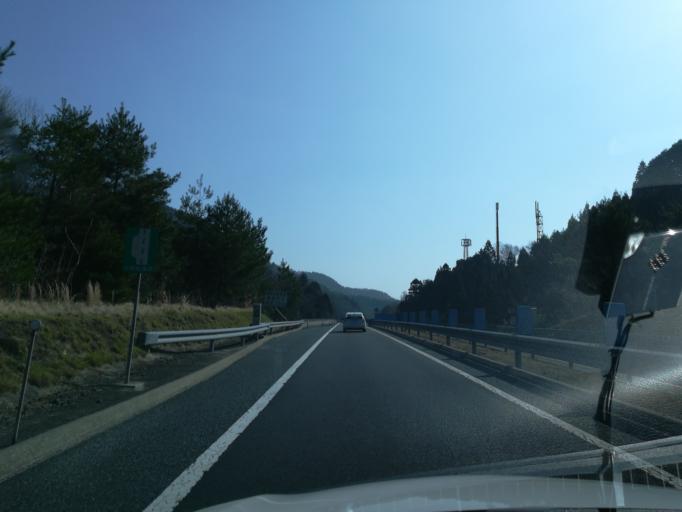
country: JP
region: Tokushima
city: Ikedacho
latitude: 34.0046
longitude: 133.6970
